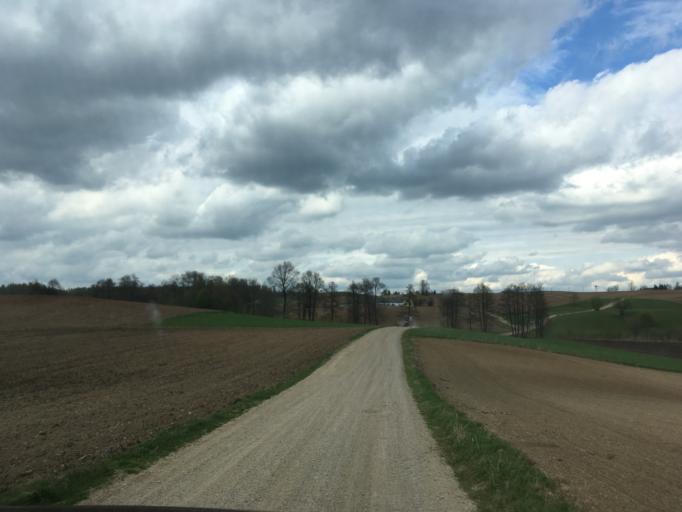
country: PL
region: Podlasie
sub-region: Powiat sejnenski
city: Punsk
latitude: 54.3804
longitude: 22.9581
